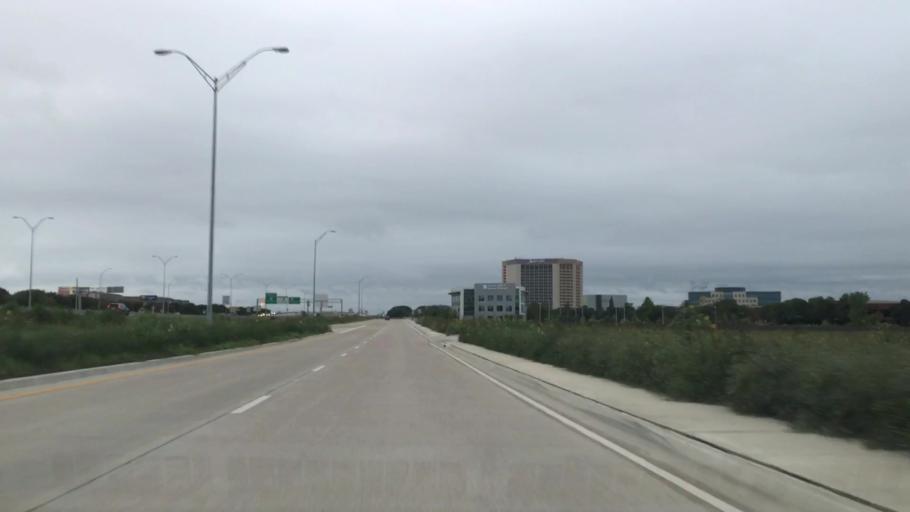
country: US
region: Texas
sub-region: Dallas County
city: Coppell
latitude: 32.9179
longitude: -97.0121
